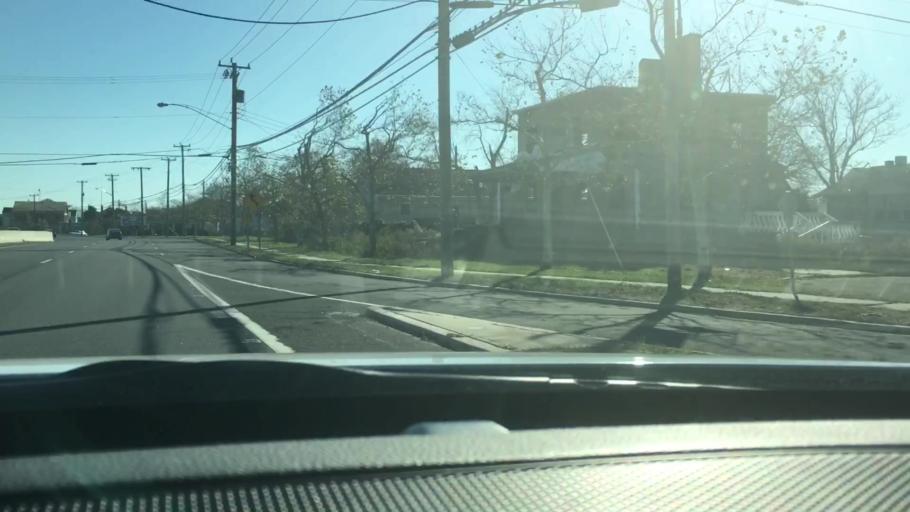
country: US
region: New Jersey
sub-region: Atlantic County
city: Pleasantville
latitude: 39.3866
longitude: -74.5154
